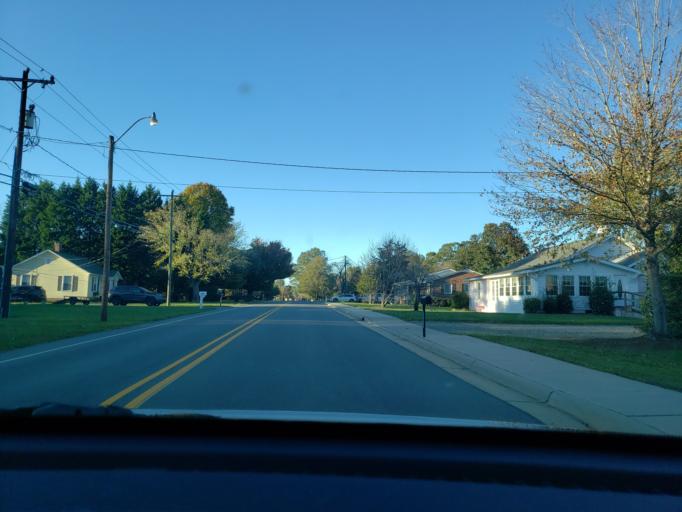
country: US
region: North Carolina
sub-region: Forsyth County
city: Walkertown
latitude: 36.1638
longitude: -80.1469
